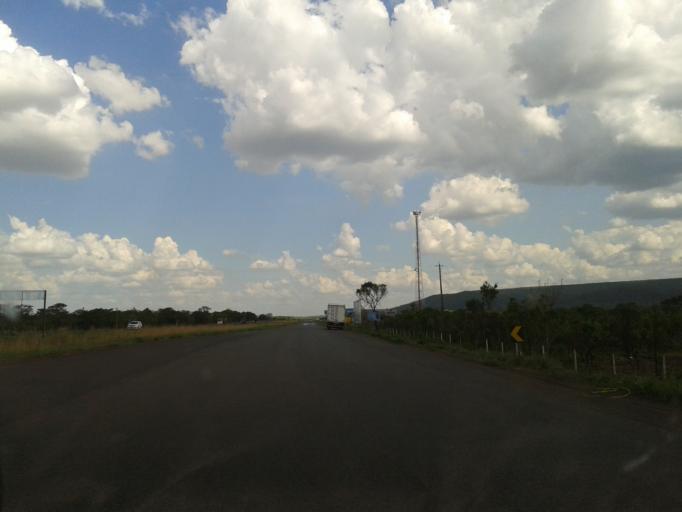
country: BR
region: Goias
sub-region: Caldas Novas
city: Caldas Novas
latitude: -17.6994
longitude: -48.7091
